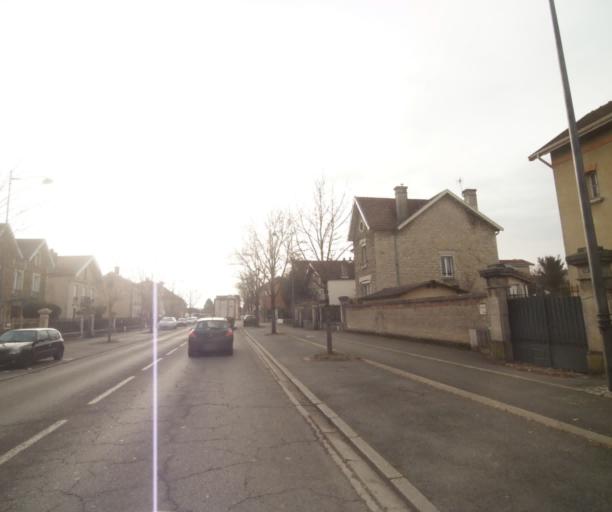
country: FR
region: Champagne-Ardenne
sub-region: Departement de la Haute-Marne
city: Saint-Dizier
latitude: 48.6307
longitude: 4.9548
